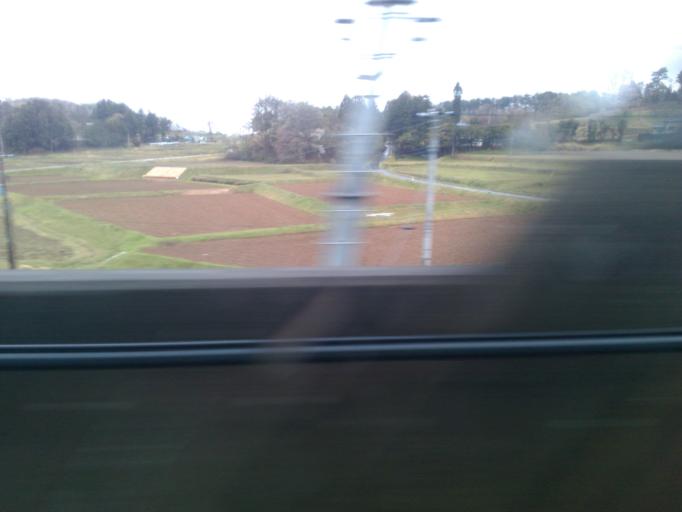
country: JP
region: Miyagi
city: Kogota
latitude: 38.7361
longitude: 141.0645
